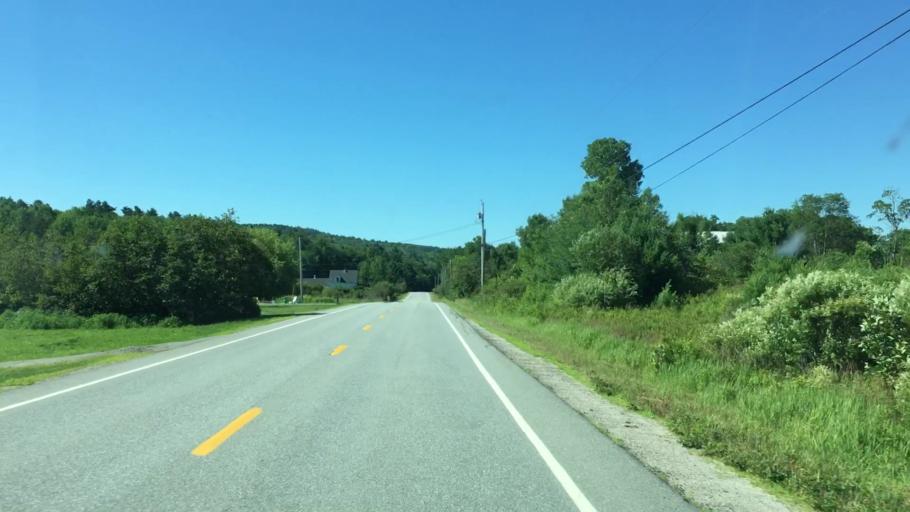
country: US
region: Maine
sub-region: Hancock County
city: Dedham
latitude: 44.6723
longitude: -68.6724
